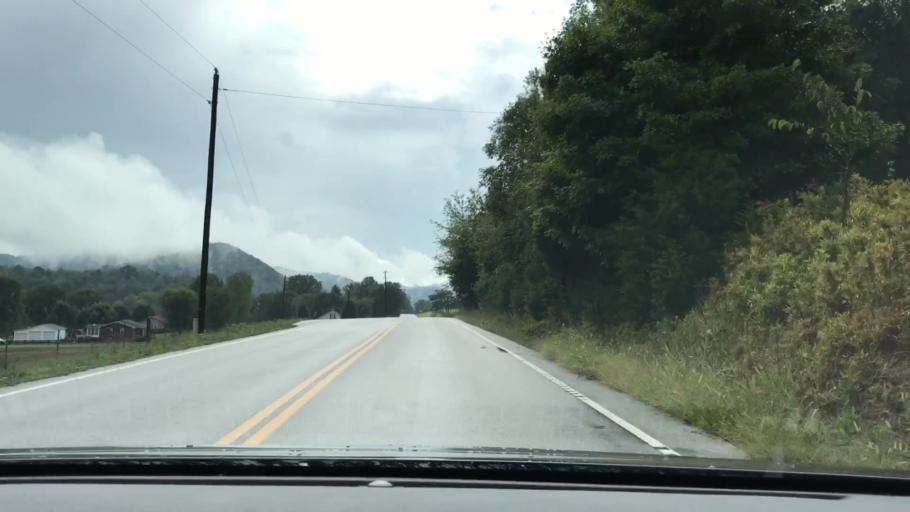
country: US
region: Tennessee
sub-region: Smith County
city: Carthage
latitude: 36.3923
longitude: -85.9477
